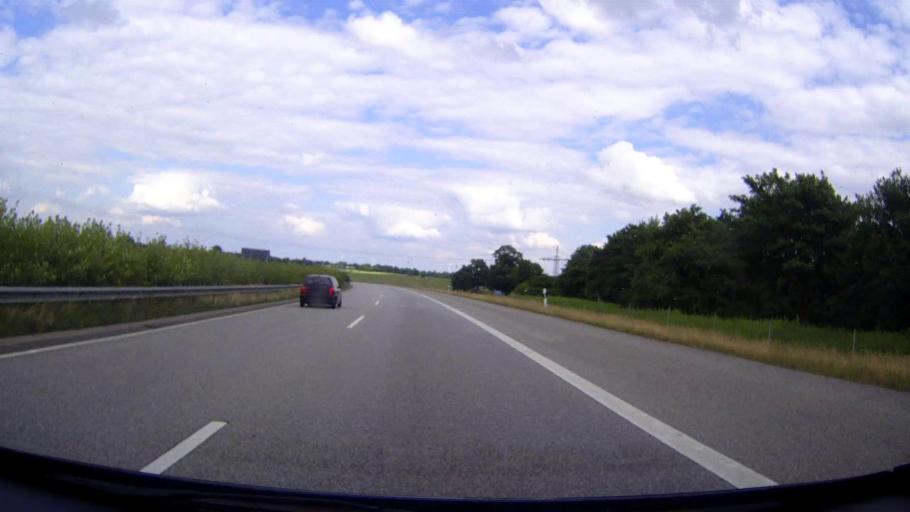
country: DE
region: Schleswig-Holstein
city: Geschendorf
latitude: 53.9235
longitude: 10.4657
